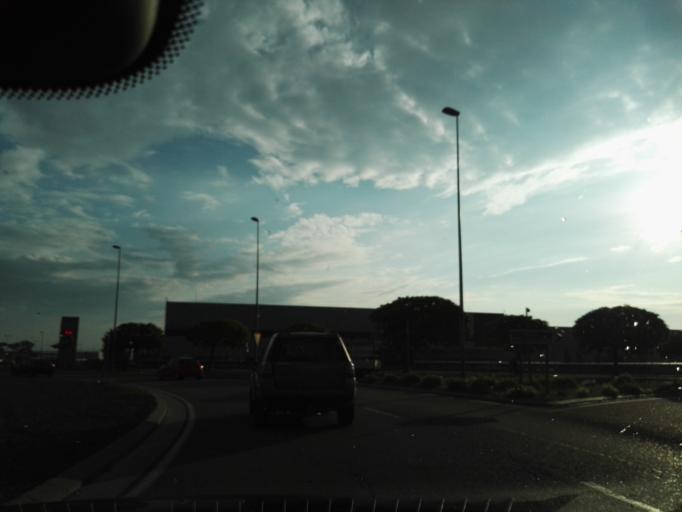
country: ES
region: Aragon
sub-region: Provincia de Zaragoza
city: Montecanal
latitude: 41.6391
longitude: -0.9918
